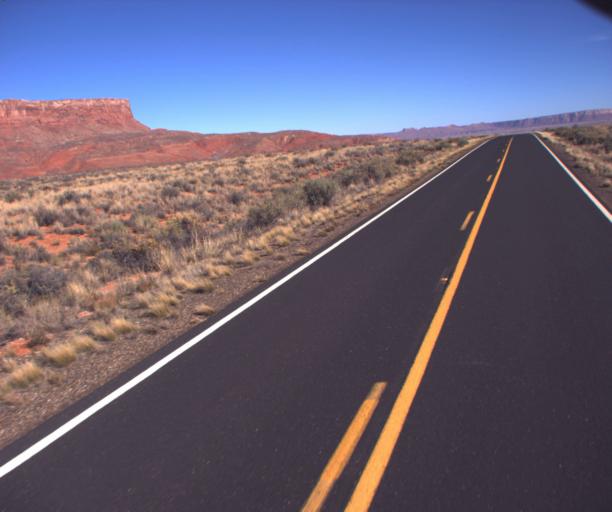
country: US
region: Arizona
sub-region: Coconino County
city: Page
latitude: 36.6939
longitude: -111.8997
